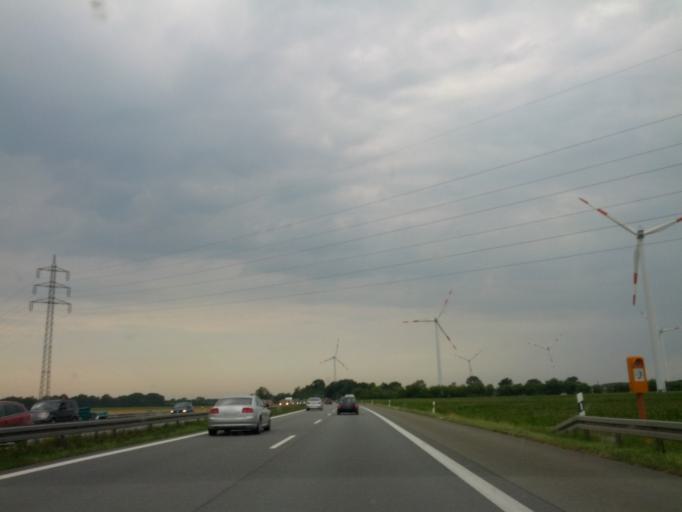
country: DE
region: Brandenburg
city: Dabergotz
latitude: 52.9311
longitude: 12.7030
